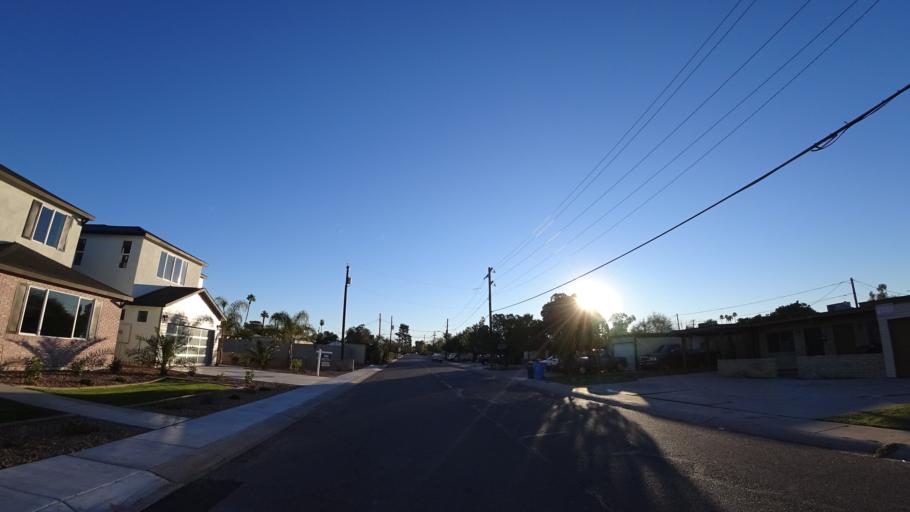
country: US
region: Arizona
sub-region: Maricopa County
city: Paradise Valley
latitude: 33.4841
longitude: -111.9976
